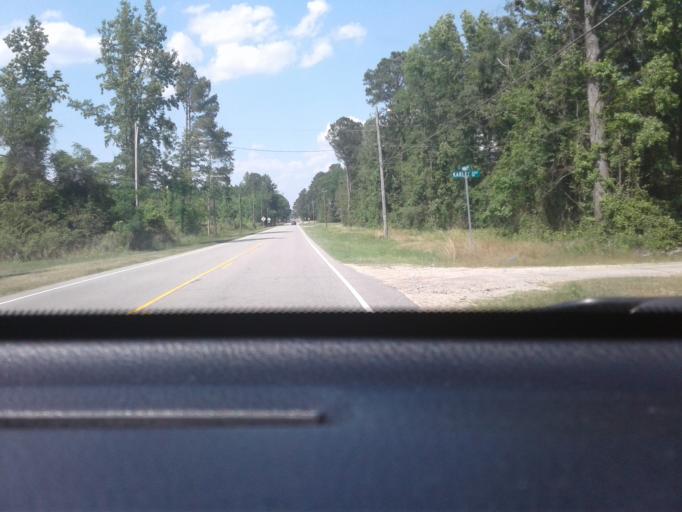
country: US
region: North Carolina
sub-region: Cumberland County
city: Eastover
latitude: 35.1691
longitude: -78.7241
